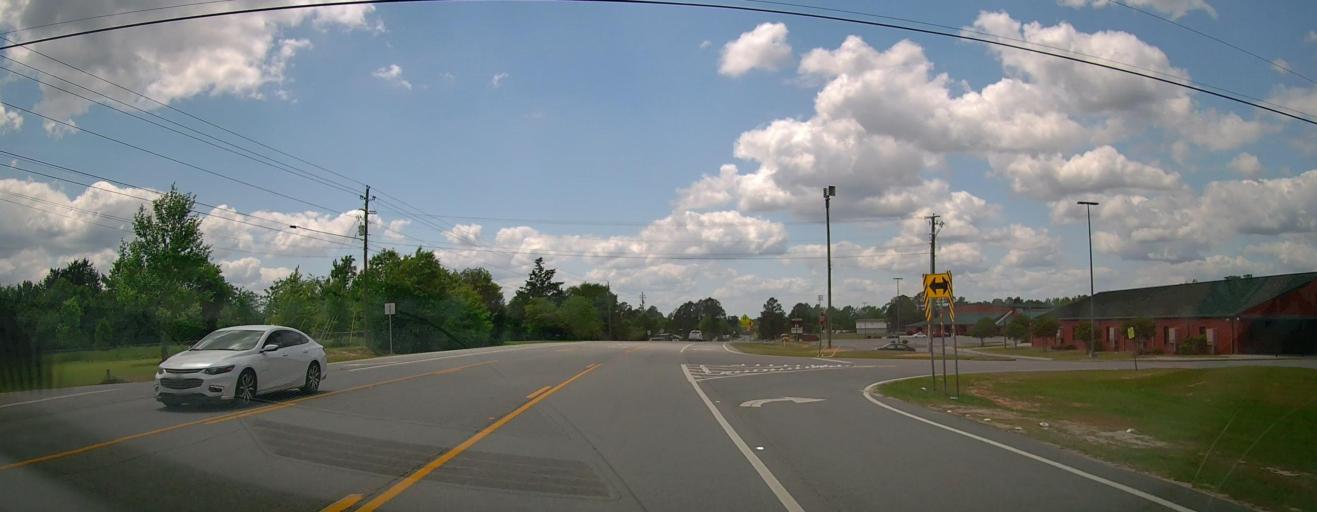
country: US
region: Georgia
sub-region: Laurens County
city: East Dublin
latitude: 32.5612
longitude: -82.8174
